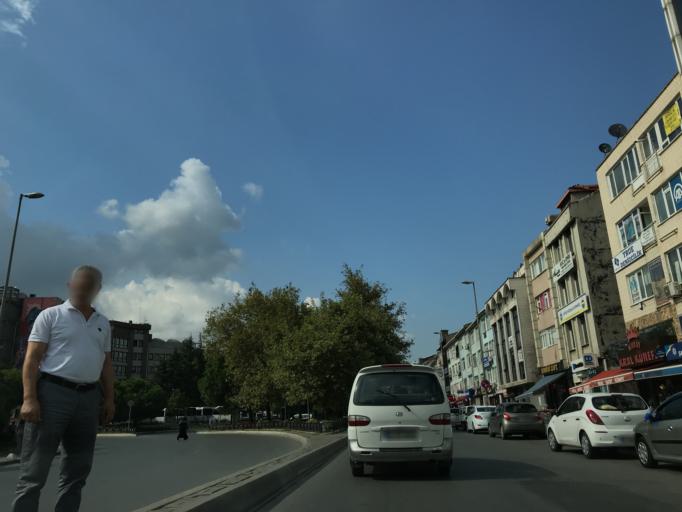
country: TR
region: Istanbul
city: UEskuedar
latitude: 40.9922
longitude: 29.0390
